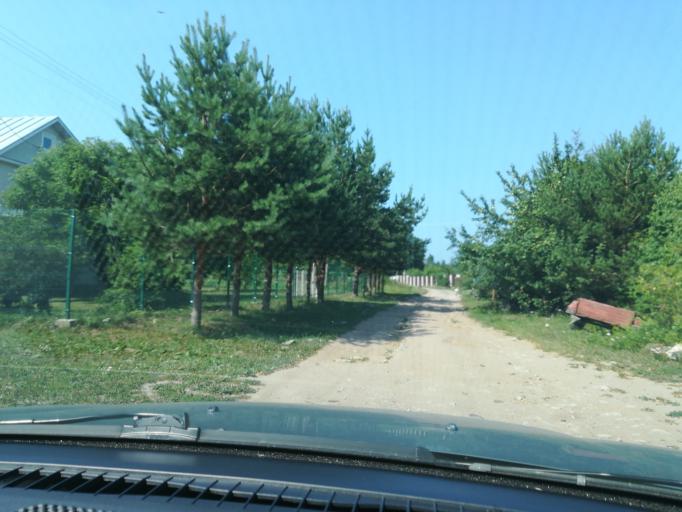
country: RU
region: Leningrad
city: Ust'-Luga
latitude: 59.7605
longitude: 28.1849
